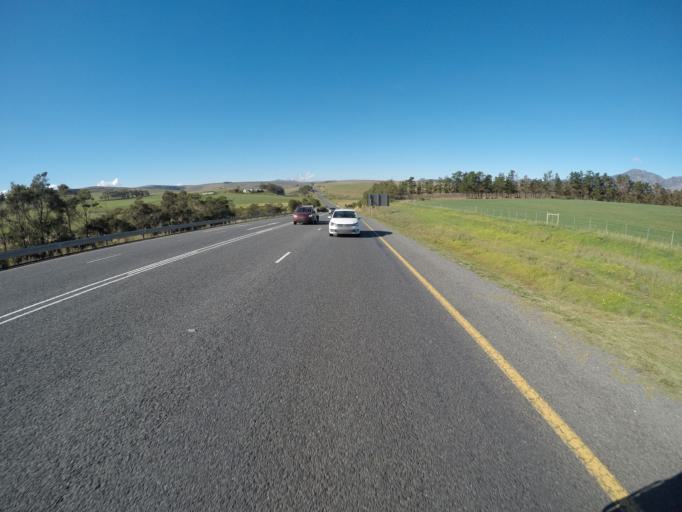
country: ZA
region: Western Cape
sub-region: Overberg District Municipality
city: Hermanus
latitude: -34.2356
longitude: 19.2117
